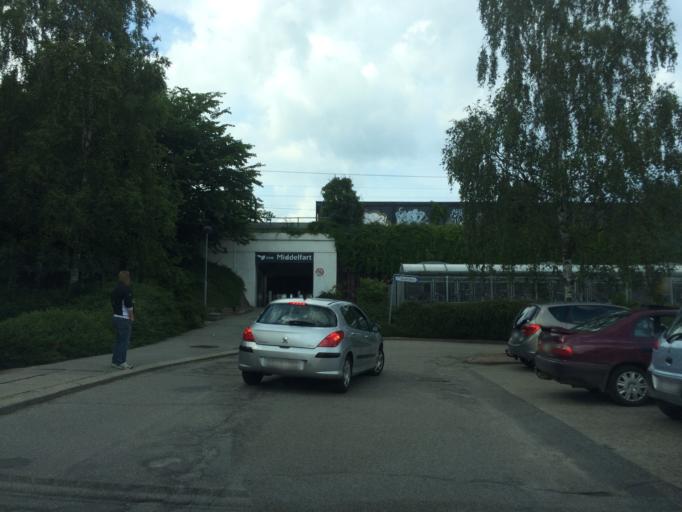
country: DK
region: South Denmark
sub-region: Middelfart Kommune
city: Middelfart
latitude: 55.5012
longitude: 9.7339
